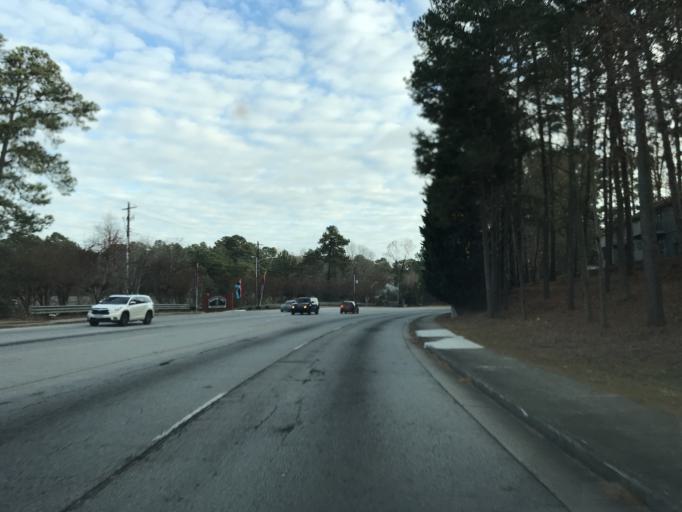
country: US
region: Georgia
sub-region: DeKalb County
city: Tucker
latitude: 33.8916
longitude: -84.2286
